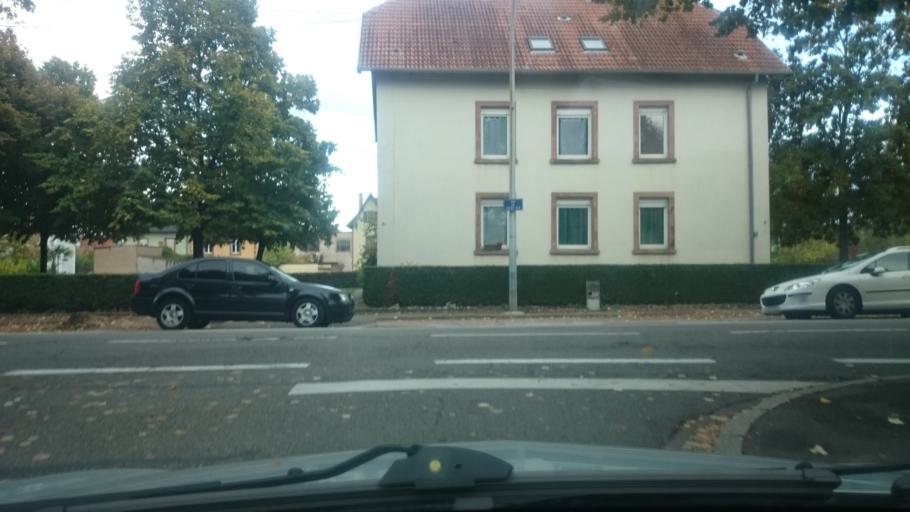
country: FR
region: Alsace
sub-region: Departement du Bas-Rhin
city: Selestat
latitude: 48.2614
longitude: 7.4405
